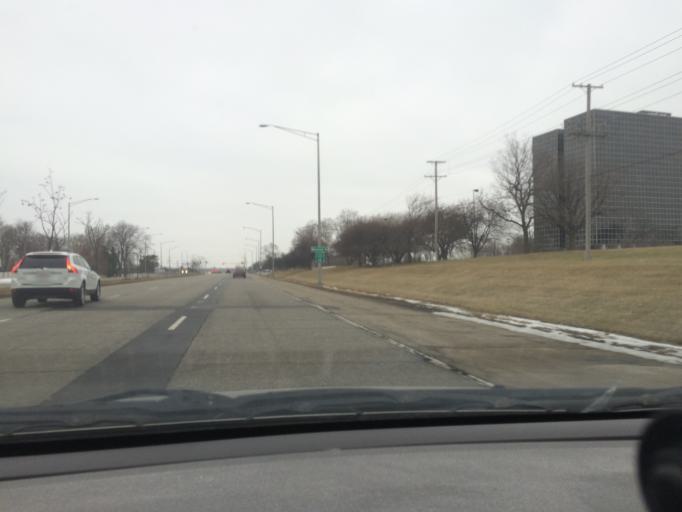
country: US
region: Illinois
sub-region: Cook County
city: Hoffman Estates
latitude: 42.0386
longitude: -88.0405
